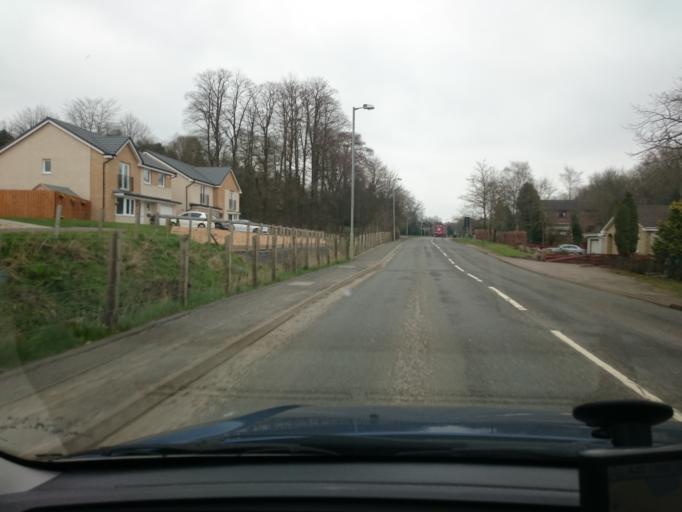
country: GB
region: Scotland
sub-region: North Lanarkshire
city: Kilsyth
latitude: 55.9797
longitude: -4.0376
